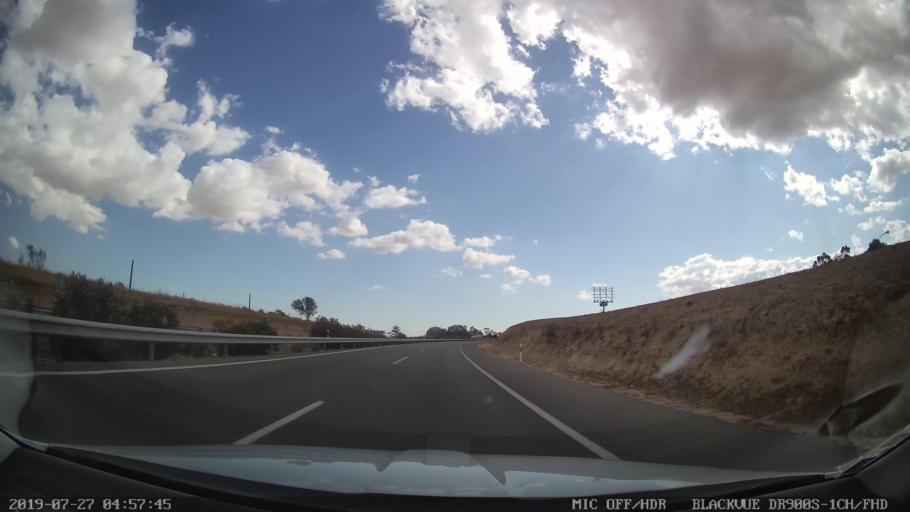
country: ES
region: Castille-La Mancha
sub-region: Province of Toledo
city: Valmojado
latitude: 40.2227
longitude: -4.0754
